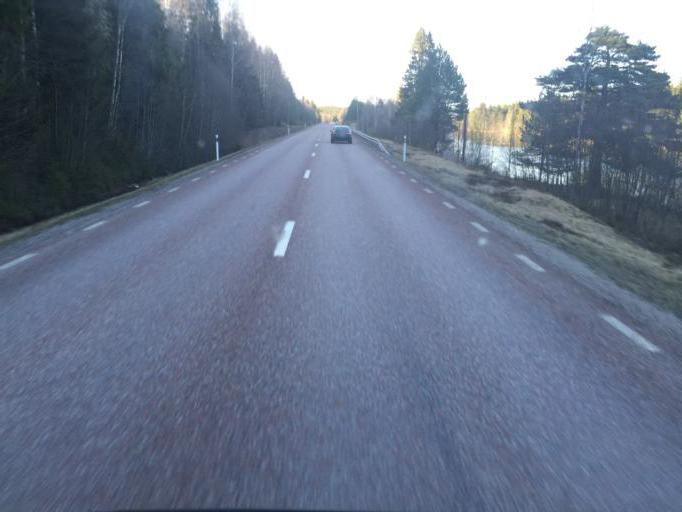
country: SE
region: Dalarna
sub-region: Gagnefs Kommun
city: Mockfjard
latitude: 60.4822
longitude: 14.7744
